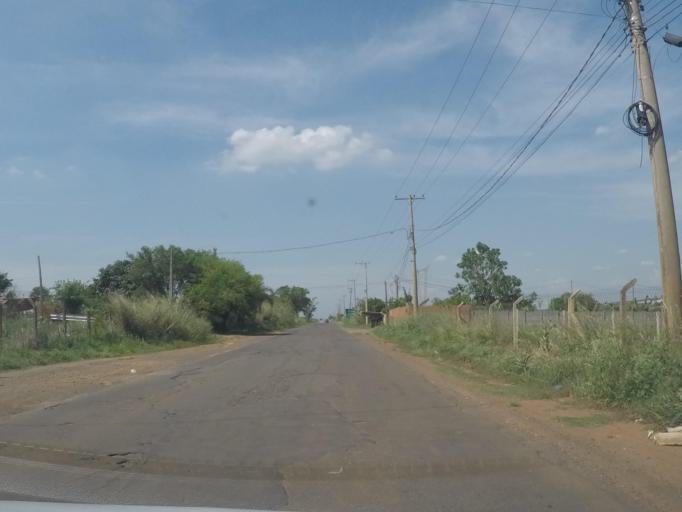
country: BR
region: Sao Paulo
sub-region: Sumare
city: Sumare
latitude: -22.8668
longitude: -47.2961
